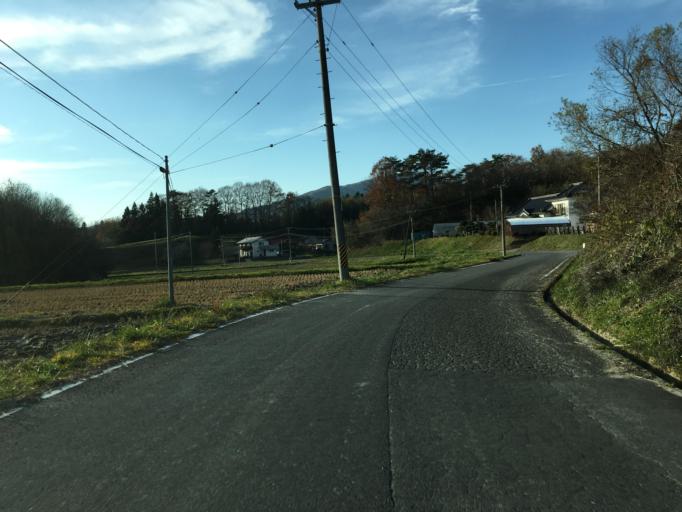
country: JP
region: Fukushima
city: Ishikawa
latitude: 37.2494
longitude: 140.5726
